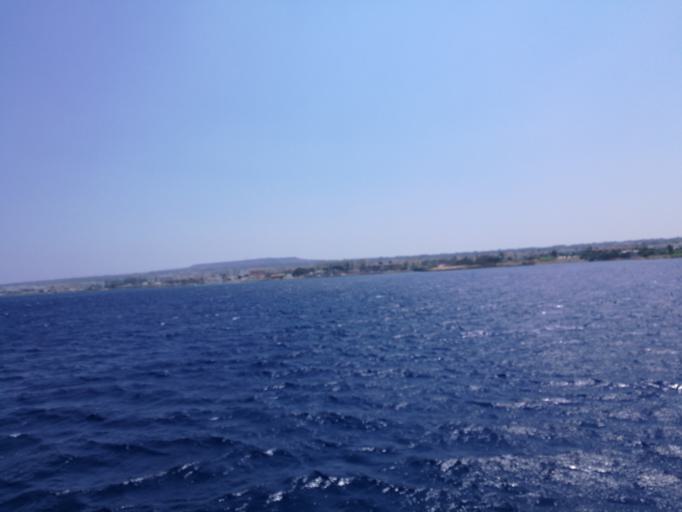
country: CY
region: Ammochostos
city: Protaras
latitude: 35.0466
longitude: 34.0409
